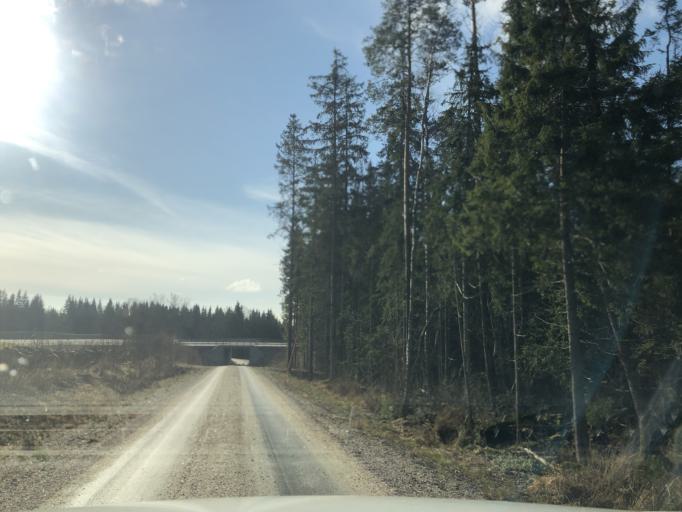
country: SE
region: Vaestra Goetaland
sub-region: Ulricehamns Kommun
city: Ulricehamn
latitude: 57.8124
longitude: 13.3805
